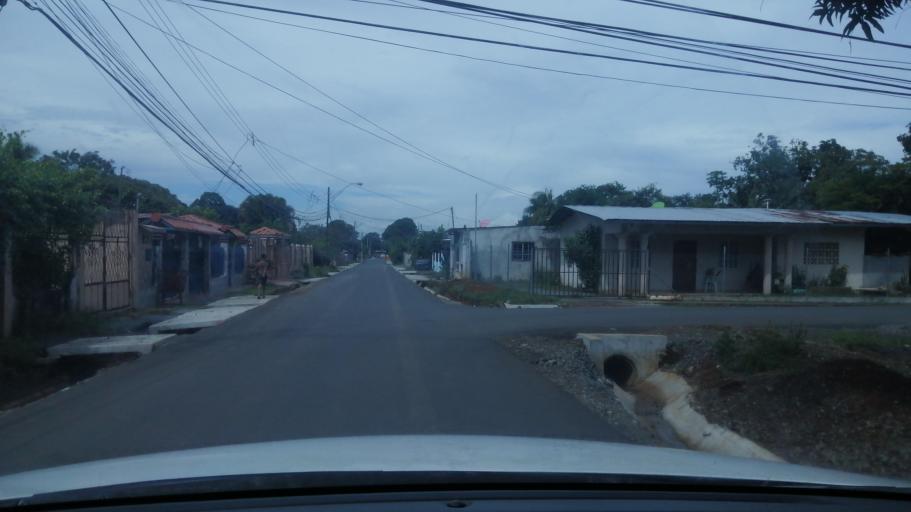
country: PA
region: Chiriqui
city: David
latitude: 8.4178
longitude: -82.4482
